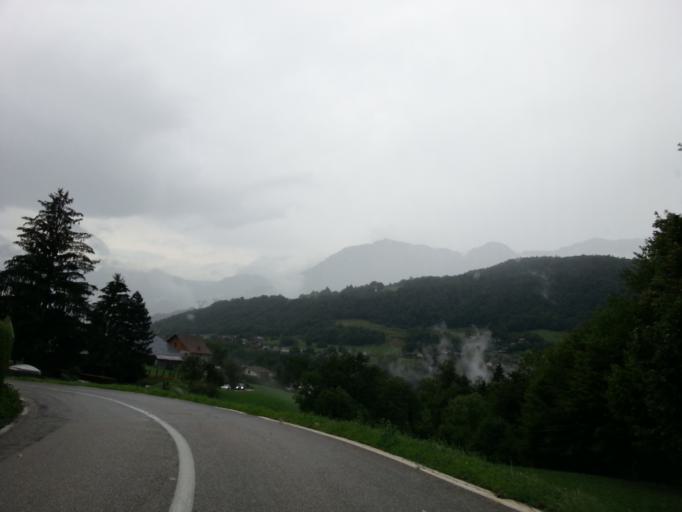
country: FR
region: Rhone-Alpes
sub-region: Departement de la Savoie
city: Albertville
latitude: 45.6903
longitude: 6.4124
